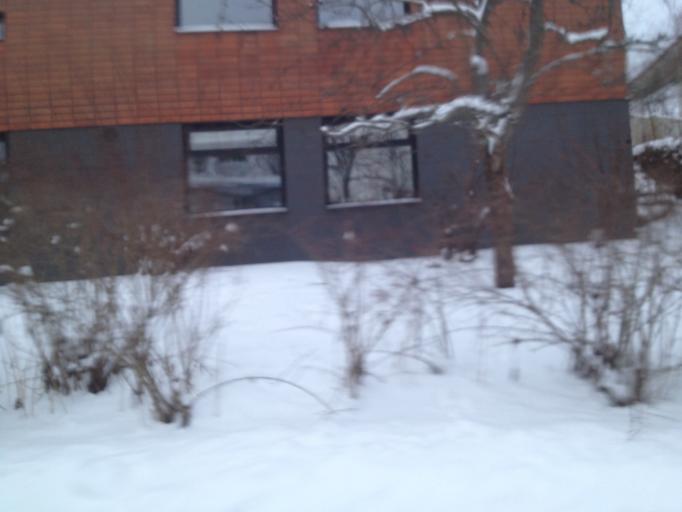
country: FI
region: Uusimaa
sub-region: Helsinki
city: Vantaa
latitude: 60.2002
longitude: 25.0740
